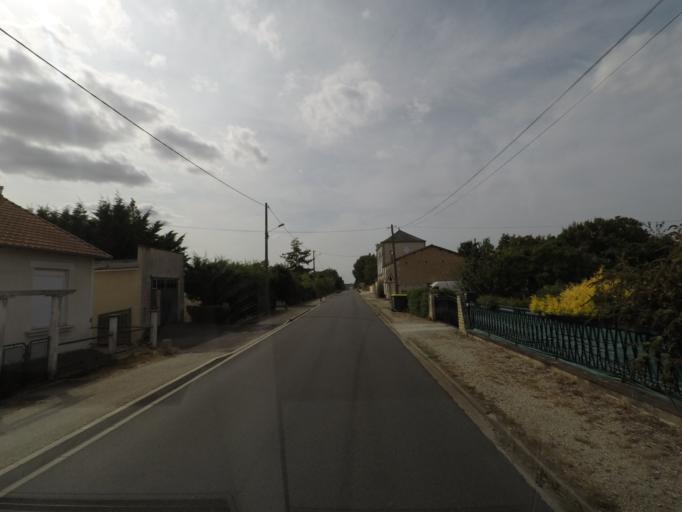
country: FR
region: Poitou-Charentes
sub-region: Departement de la Charente
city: Ruffec
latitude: 46.0266
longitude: 0.2131
